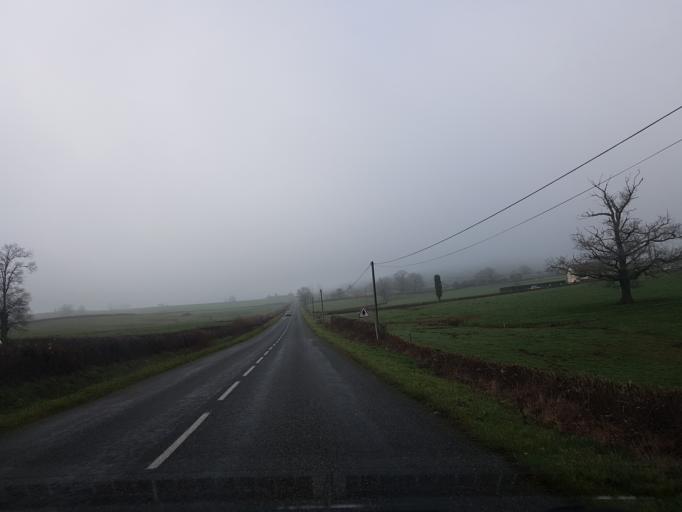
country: FR
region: Bourgogne
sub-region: Departement de Saone-et-Loire
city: Saint-Berain-sous-Sanvignes
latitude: 46.7288
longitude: 4.3100
